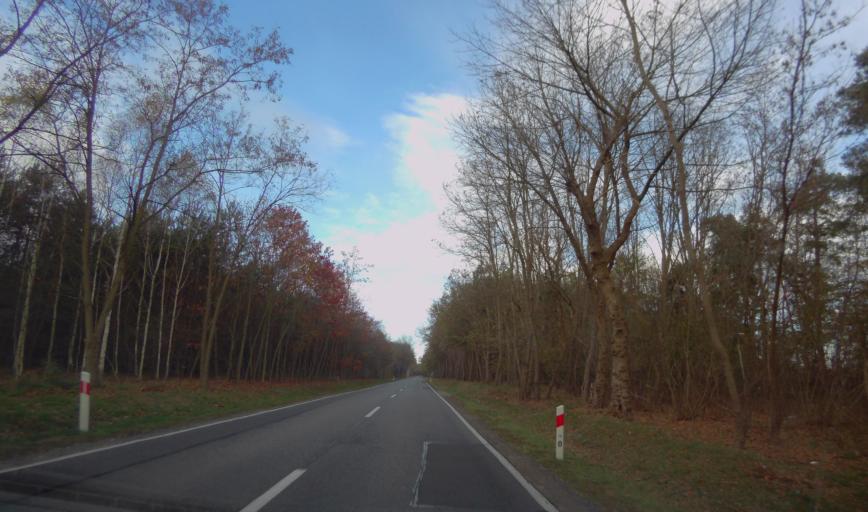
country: PL
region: Subcarpathian Voivodeship
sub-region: Powiat nizanski
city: Krzeszow
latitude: 50.3768
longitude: 22.3115
